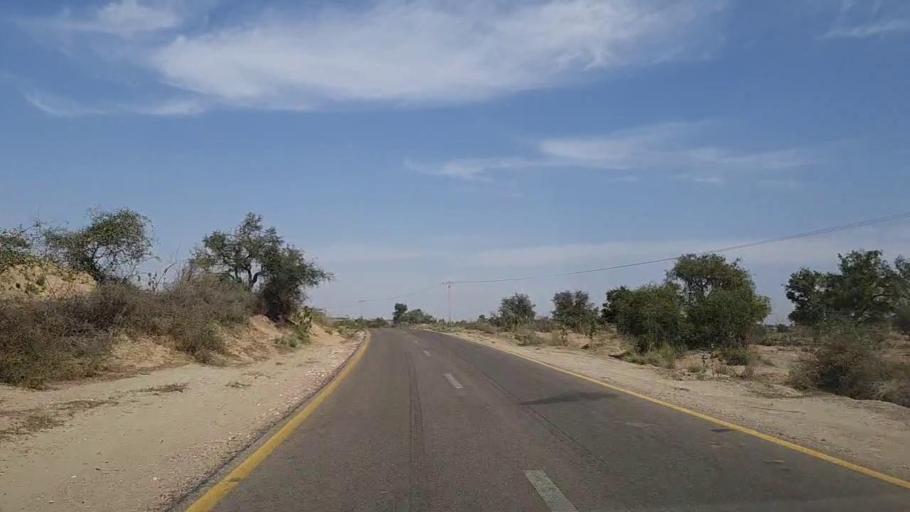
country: PK
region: Sindh
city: Mithi
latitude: 24.7935
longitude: 69.8146
